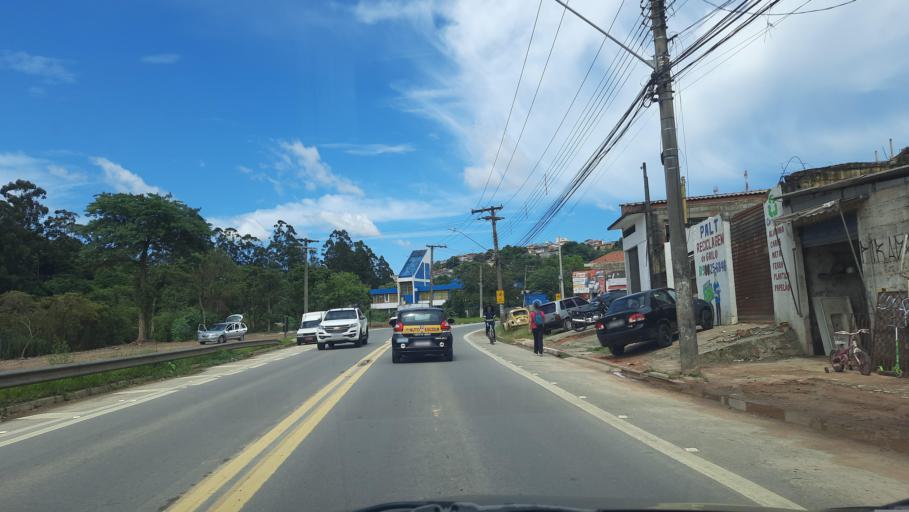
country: BR
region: Sao Paulo
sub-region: Franco Da Rocha
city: Franco da Rocha
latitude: -23.3316
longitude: -46.7141
